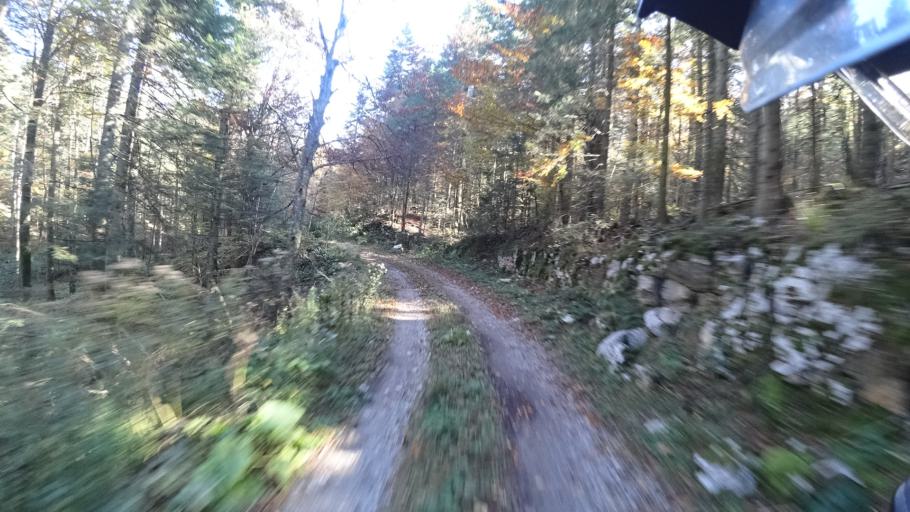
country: HR
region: Karlovacka
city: Plaski
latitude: 45.0437
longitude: 15.3353
